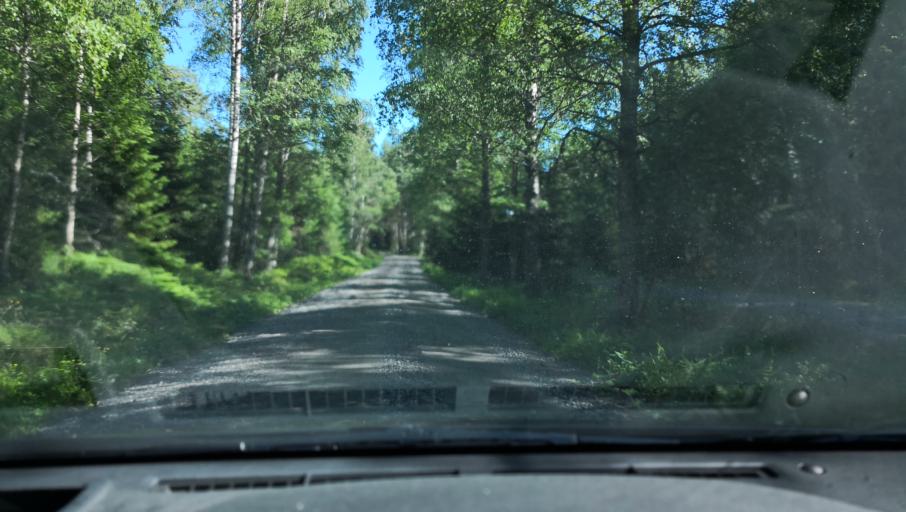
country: SE
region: Soedermanland
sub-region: Eskilstuna Kommun
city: Eskilstuna
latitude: 59.3303
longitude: 16.5811
